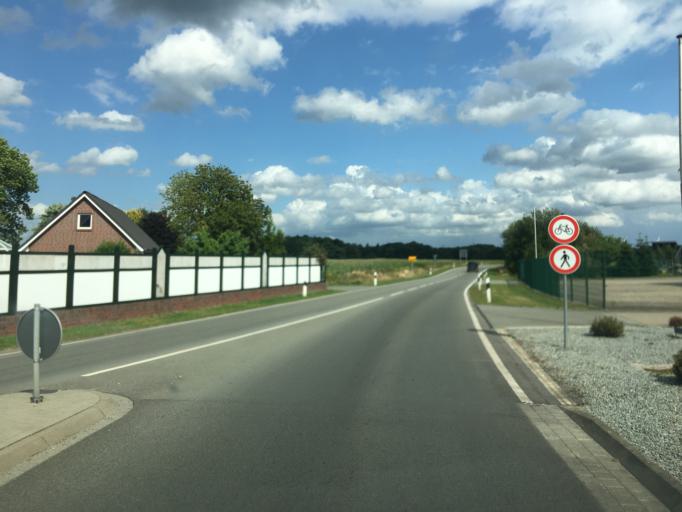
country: DE
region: Lower Saxony
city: Friesoythe
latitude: 53.0325
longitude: 7.8559
